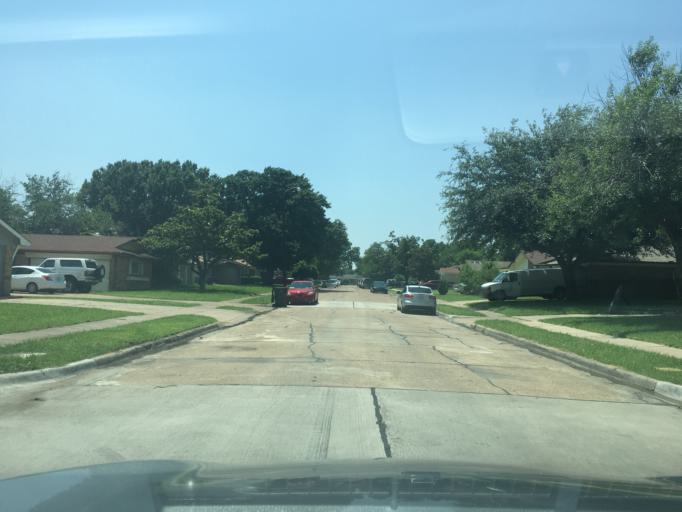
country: US
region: Texas
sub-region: Dallas County
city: Richardson
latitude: 32.9233
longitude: -96.7030
